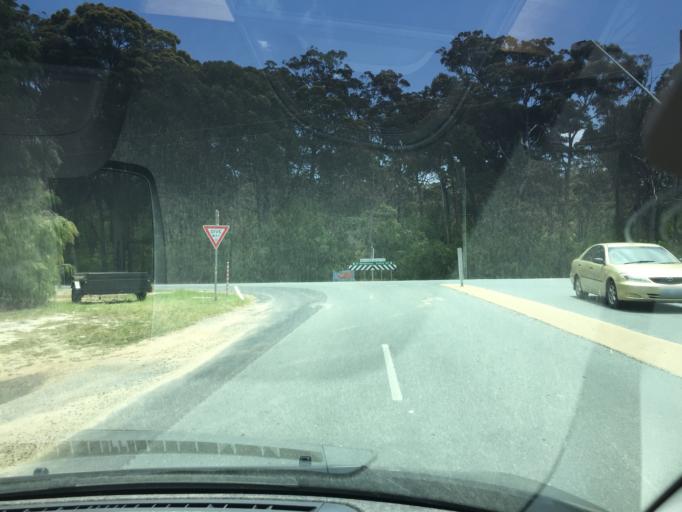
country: AU
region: New South Wales
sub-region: Bega Valley
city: Merimbula
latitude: -36.8628
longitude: 149.9123
